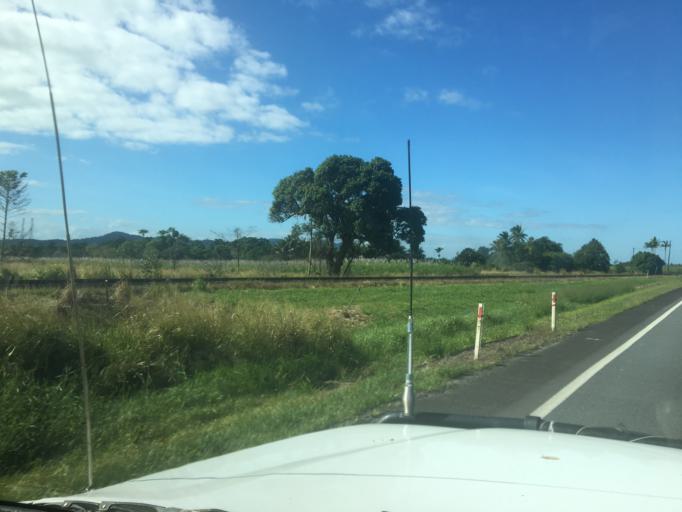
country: AU
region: Queensland
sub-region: Cassowary Coast
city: Innisfail
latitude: -17.3242
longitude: 145.9285
